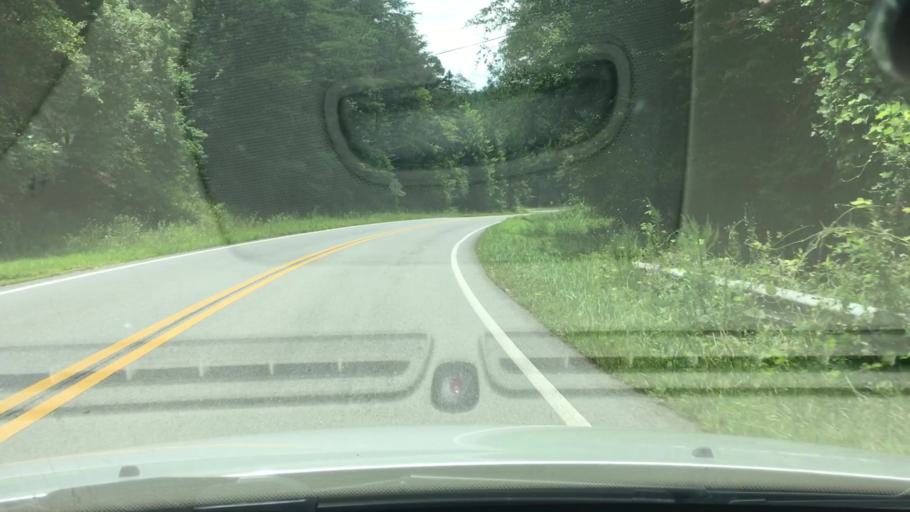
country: US
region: Georgia
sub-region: Lumpkin County
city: Dahlonega
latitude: 34.5816
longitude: -83.8860
